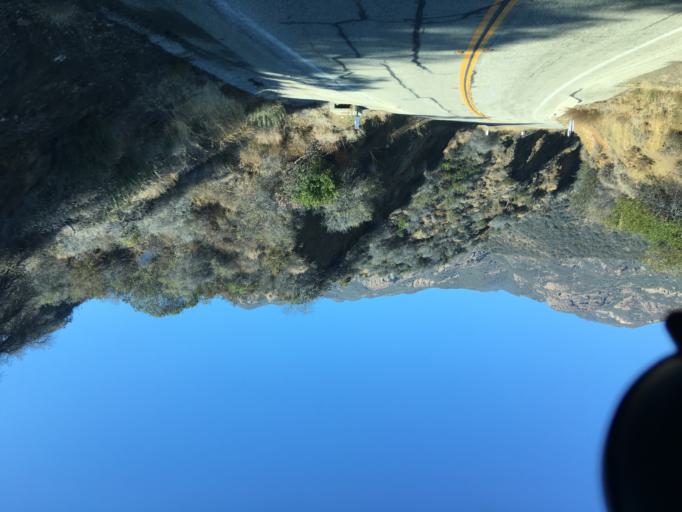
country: US
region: California
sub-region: Ventura County
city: Casa Conejo
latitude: 34.0880
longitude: -118.9017
